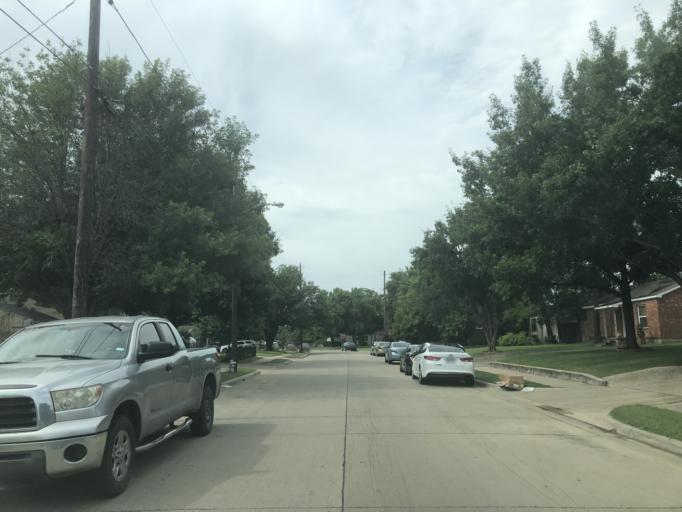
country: US
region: Texas
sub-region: Dallas County
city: Irving
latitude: 32.8115
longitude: -96.9537
